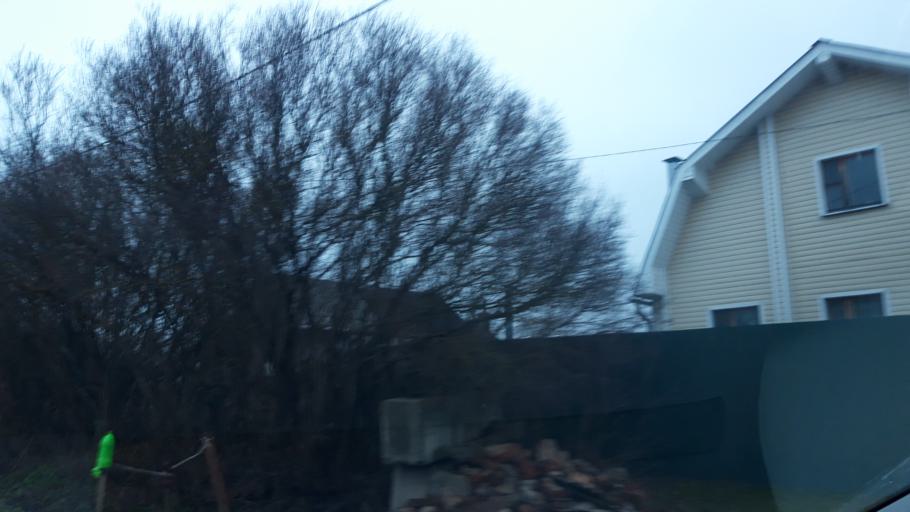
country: RU
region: Moskovskaya
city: Solnechnogorsk
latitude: 56.1222
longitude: 36.9330
